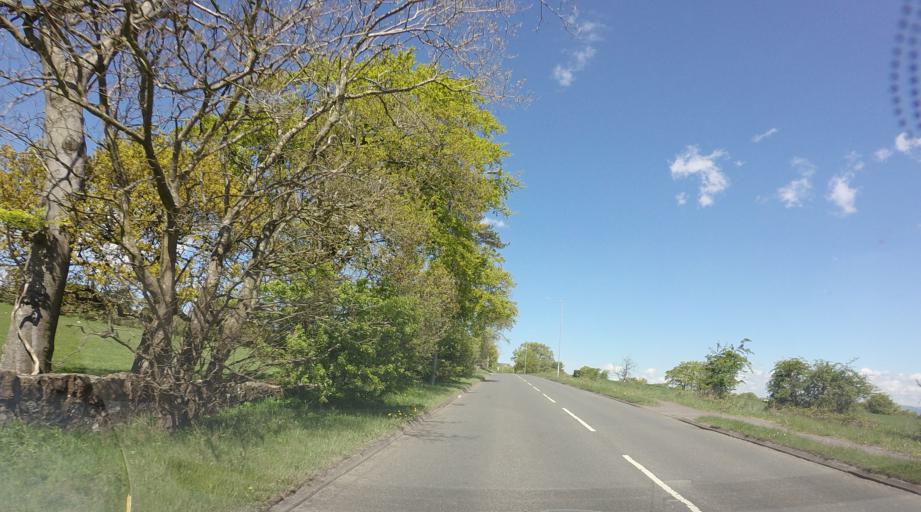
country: GB
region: Scotland
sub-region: Falkirk
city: Polmont
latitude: 55.9628
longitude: -3.6930
